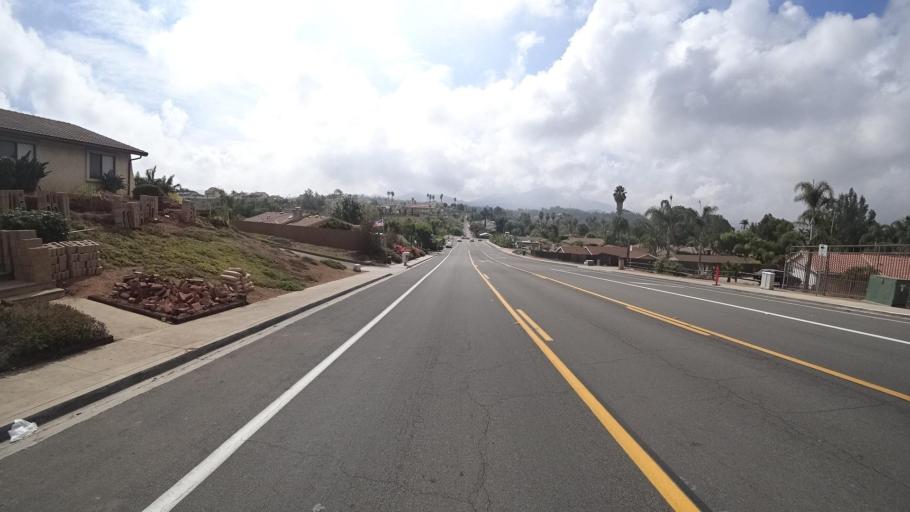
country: US
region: California
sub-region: San Diego County
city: Rancho San Diego
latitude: 32.7641
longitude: -116.9149
